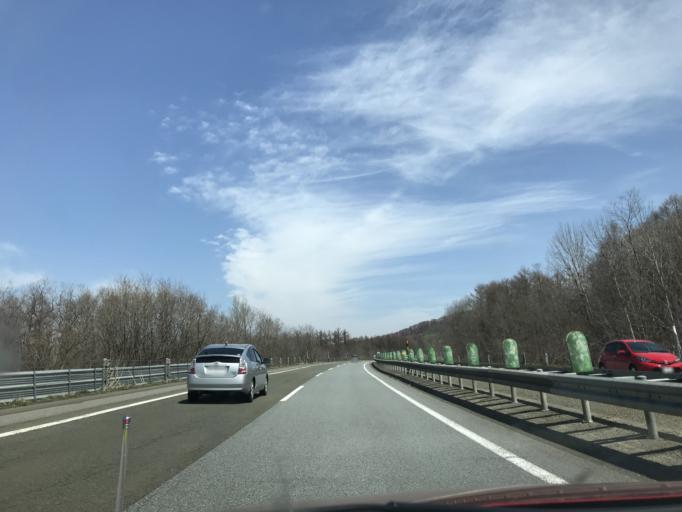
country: JP
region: Hokkaido
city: Bibai
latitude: 43.2936
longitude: 141.8669
